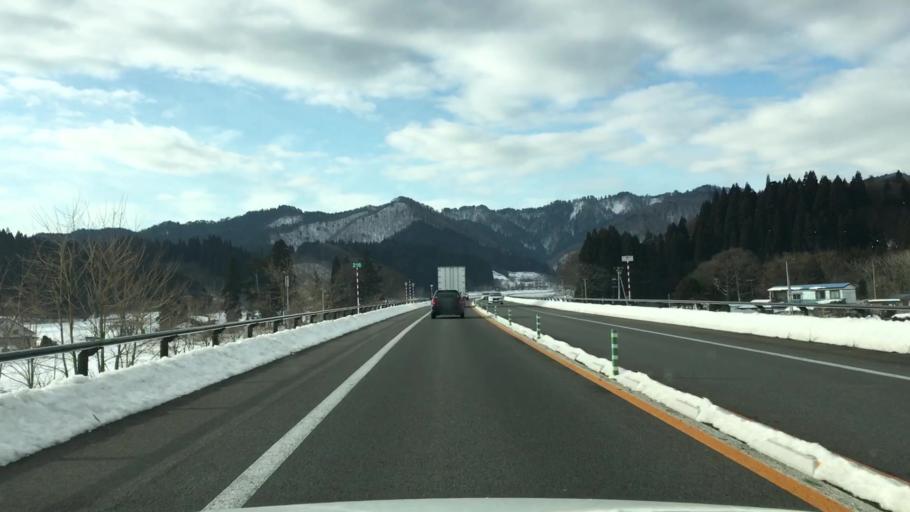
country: JP
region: Akita
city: Odate
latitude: 40.2386
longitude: 140.5037
